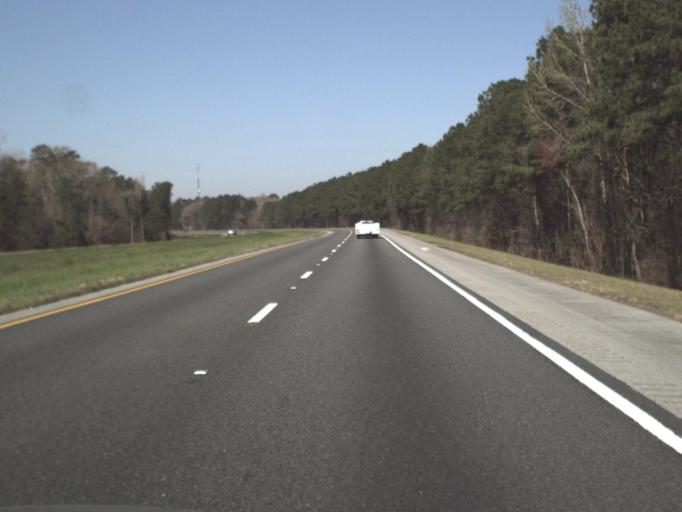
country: US
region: Florida
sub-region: Jackson County
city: Sneads
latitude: 30.6378
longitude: -84.9145
